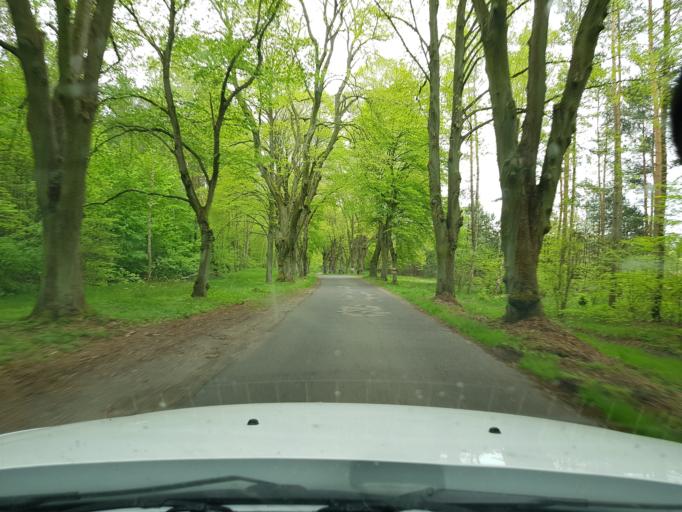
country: PL
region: West Pomeranian Voivodeship
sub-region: Powiat mysliborski
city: Debno
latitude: 52.6970
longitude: 14.6749
